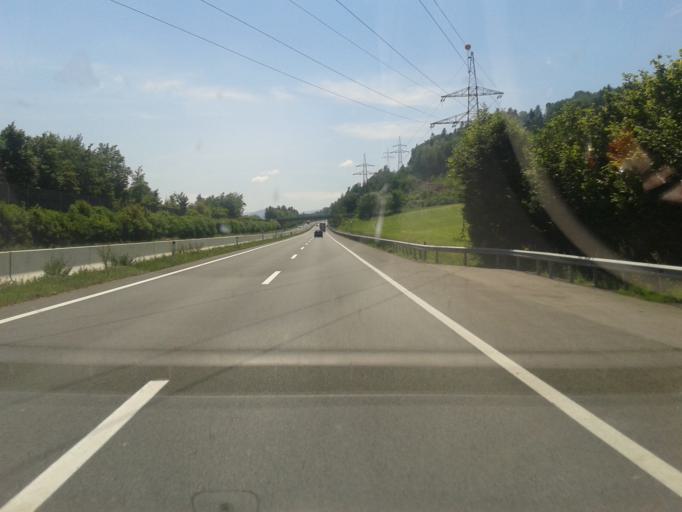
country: AT
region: Carinthia
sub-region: Politischer Bezirk Wolfsberg
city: Sankt Andrae
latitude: 46.7678
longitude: 14.8123
